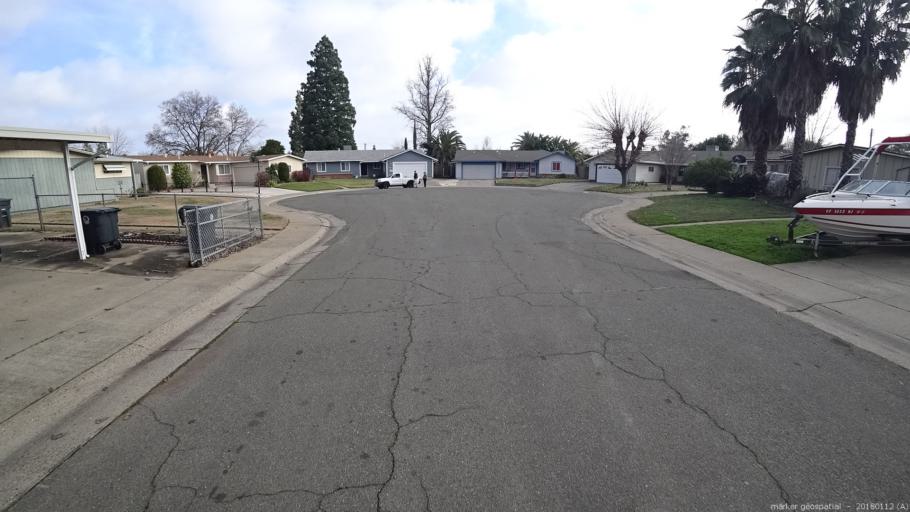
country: US
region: California
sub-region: Sacramento County
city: Rancho Cordova
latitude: 38.6015
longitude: -121.2997
